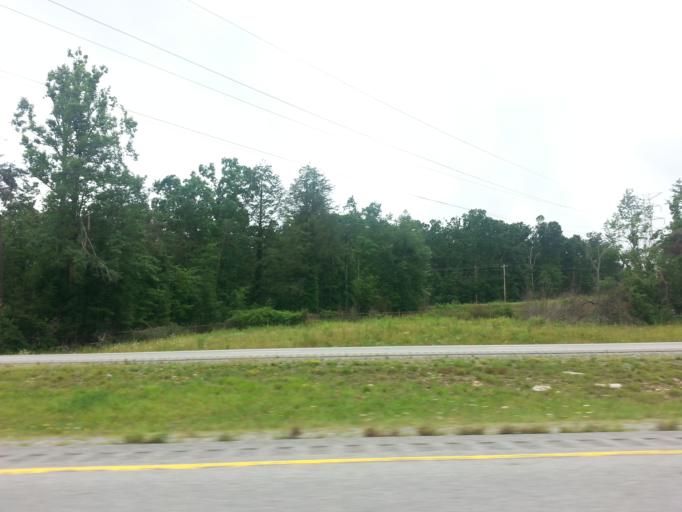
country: US
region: Tennessee
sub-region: Putnam County
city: Monterey
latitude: 36.1342
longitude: -85.2615
